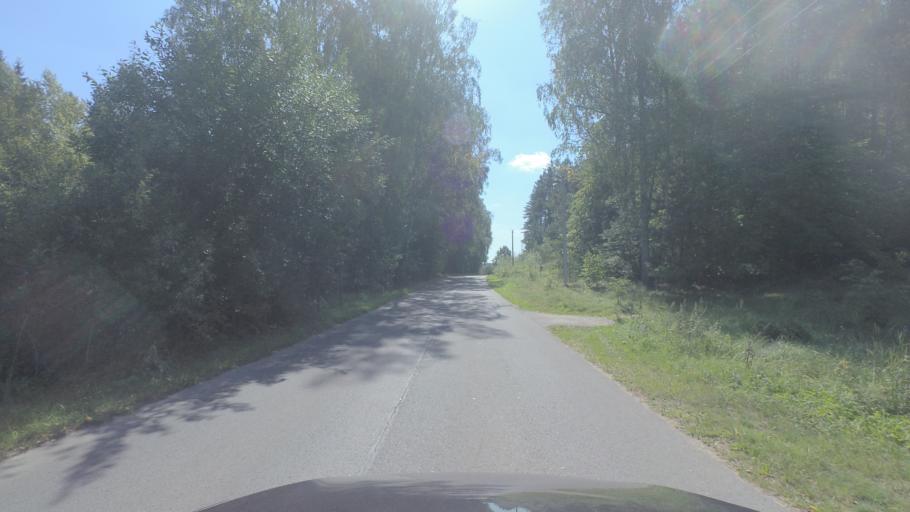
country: LT
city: Nemencine
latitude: 54.8446
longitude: 25.3725
